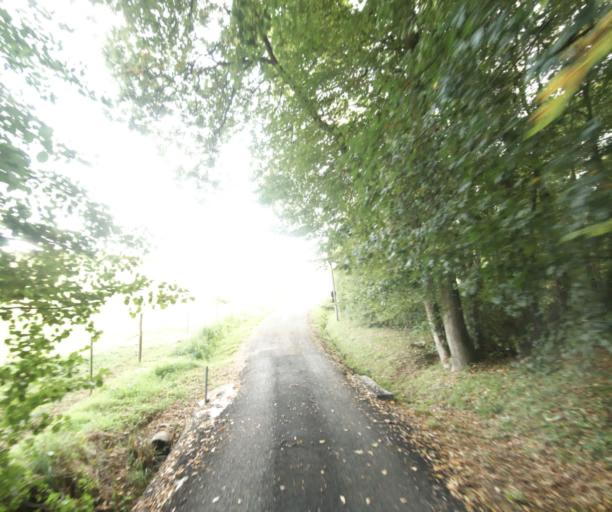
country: FR
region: Midi-Pyrenees
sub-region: Departement du Gers
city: Eauze
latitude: 43.8249
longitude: 0.1425
